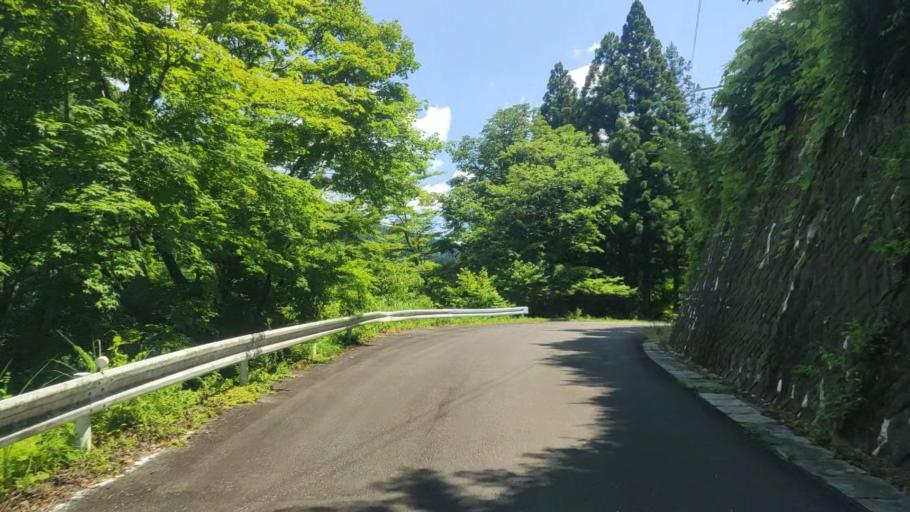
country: JP
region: Fukui
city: Ono
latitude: 35.7318
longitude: 136.5781
